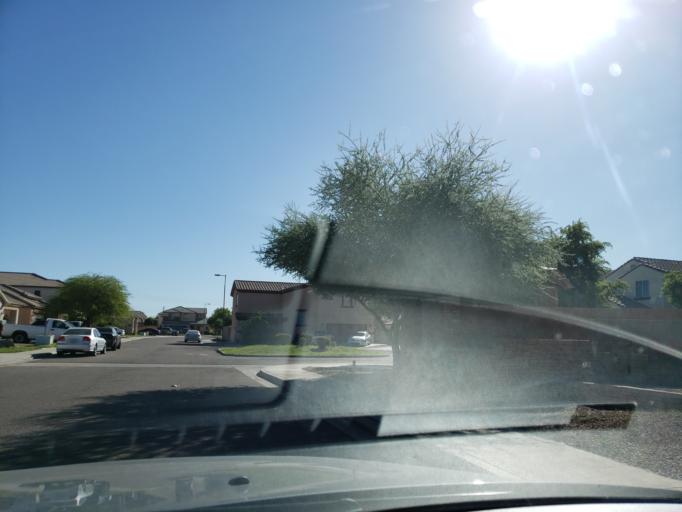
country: US
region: Arizona
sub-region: Maricopa County
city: Glendale
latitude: 33.5062
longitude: -112.2203
